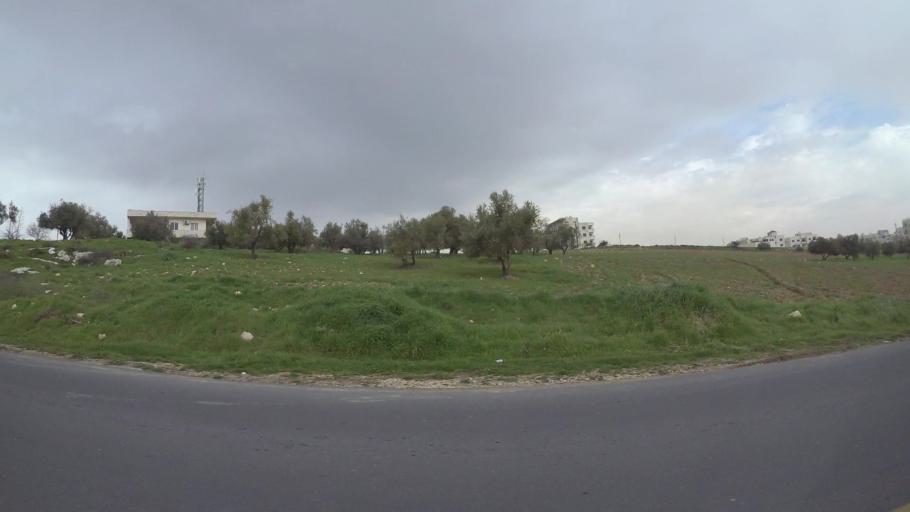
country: JO
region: Amman
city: Umm as Summaq
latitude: 31.9083
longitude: 35.8387
